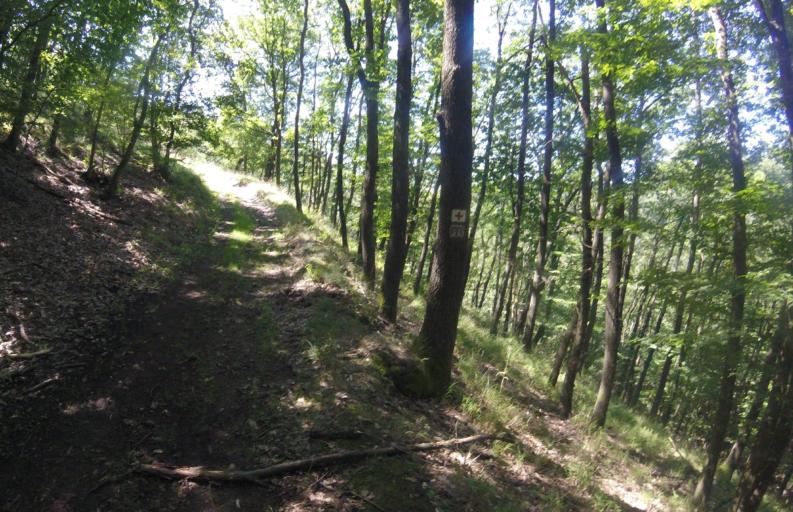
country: HU
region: Pest
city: Szob
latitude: 47.8868
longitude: 18.8696
